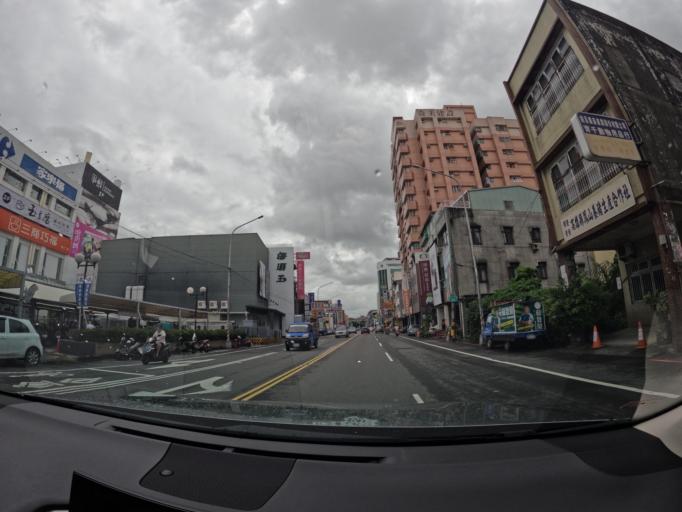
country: TW
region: Taiwan
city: Fengshan
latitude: 22.6279
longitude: 120.3478
